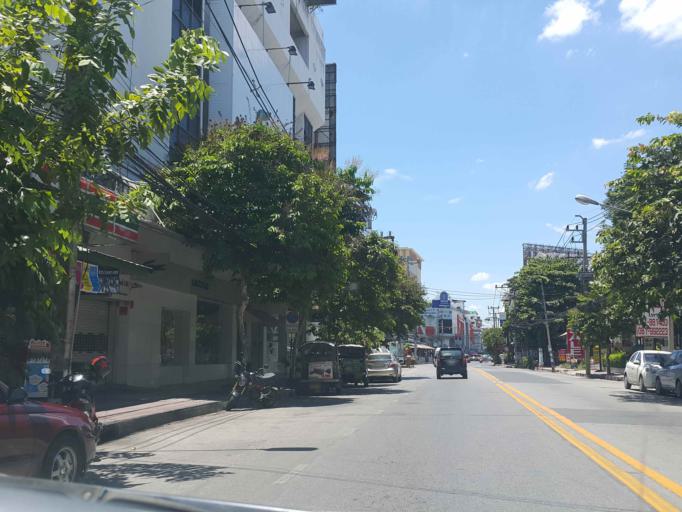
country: TH
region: Chiang Mai
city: Chiang Mai
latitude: 18.7794
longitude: 98.9995
